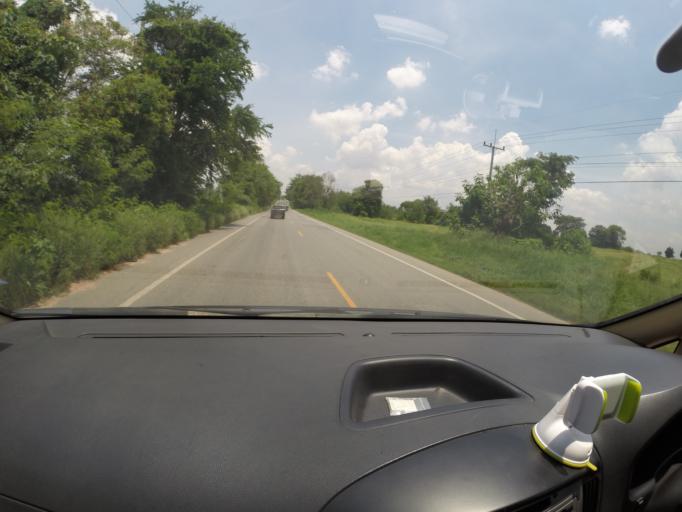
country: TH
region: Nakhon Ratchasima
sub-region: Amphoe Thepharak
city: Thepharak
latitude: 15.1258
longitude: 101.5425
